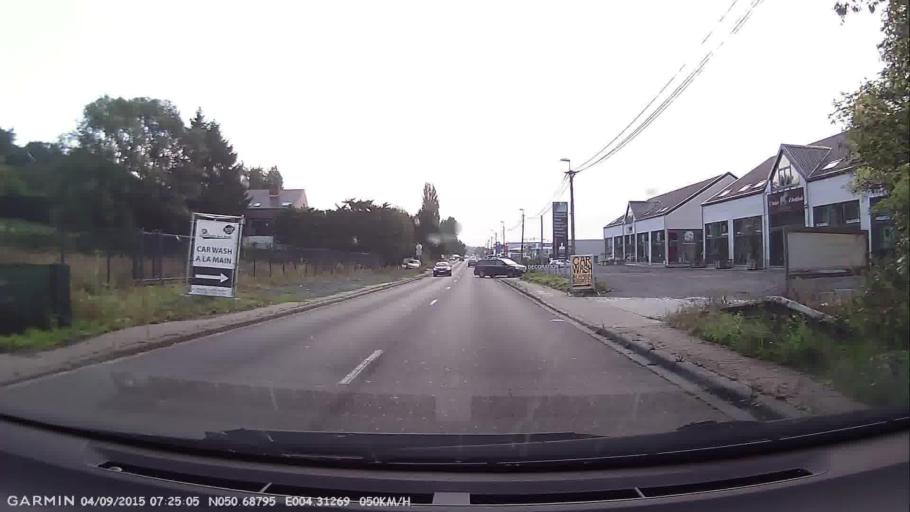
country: BE
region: Wallonia
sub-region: Province du Brabant Wallon
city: Braine-le-Chateau
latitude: 50.6881
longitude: 4.3130
